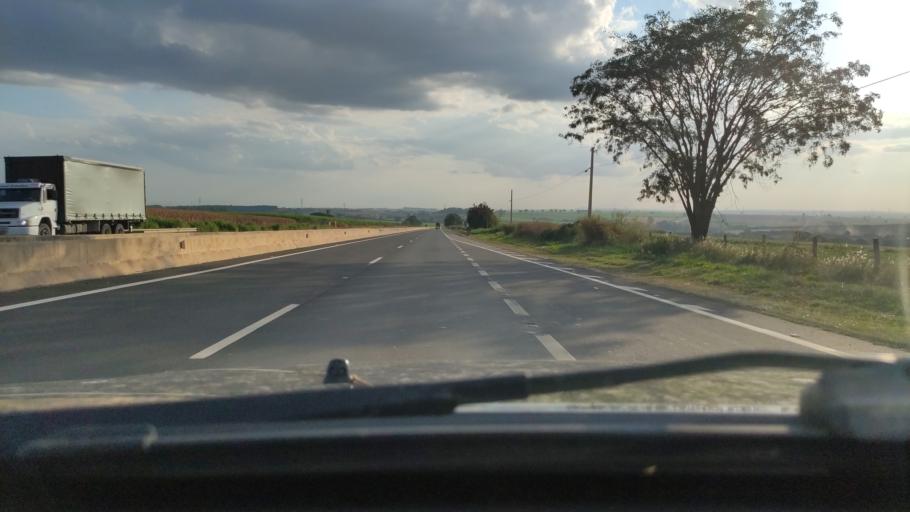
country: BR
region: Sao Paulo
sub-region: Artur Nogueira
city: Artur Nogueira
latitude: -22.4710
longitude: -47.1193
